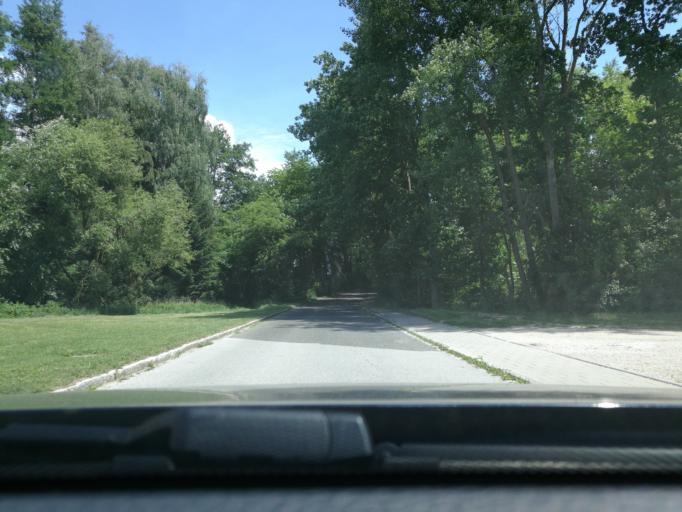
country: DE
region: Bavaria
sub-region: Regierungsbezirk Mittelfranken
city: Schwarzenbruck
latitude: 49.3549
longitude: 11.2339
